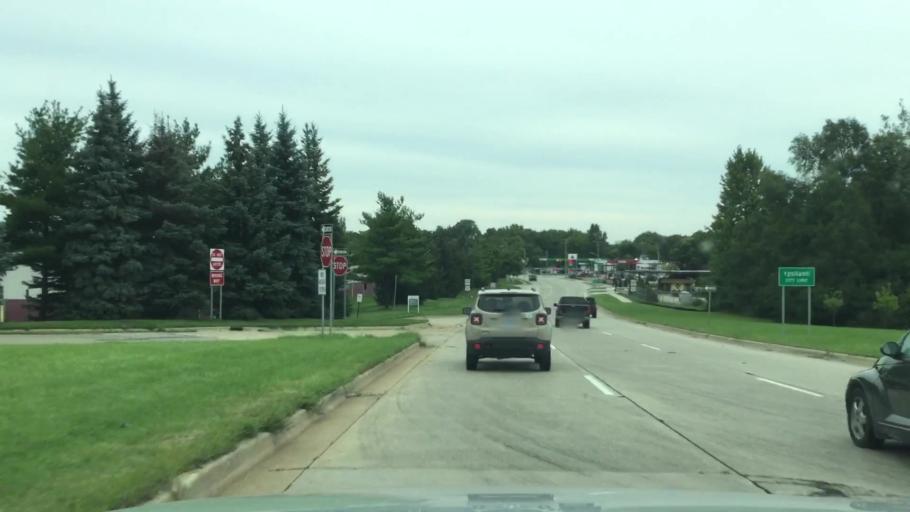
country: US
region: Michigan
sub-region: Washtenaw County
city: Ypsilanti
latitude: 42.2310
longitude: -83.6159
